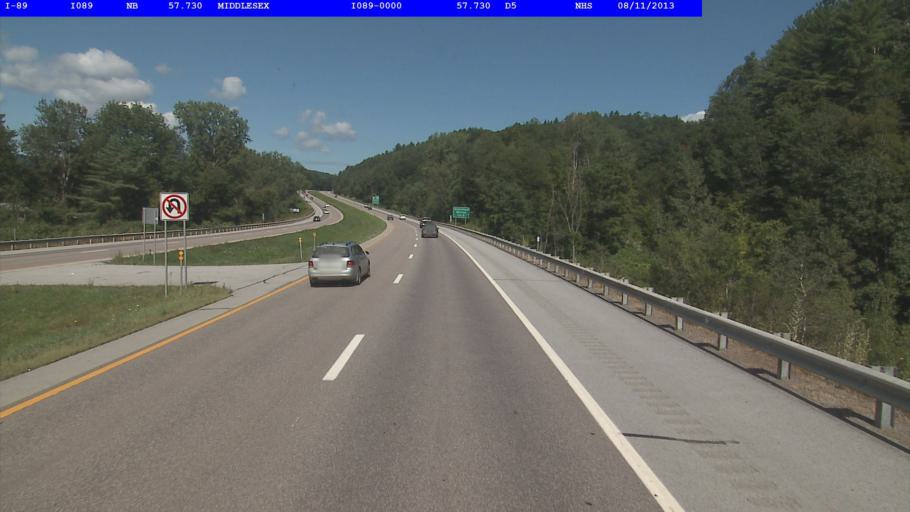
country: US
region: Vermont
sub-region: Washington County
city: Montpelier
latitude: 44.2911
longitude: -72.6681
